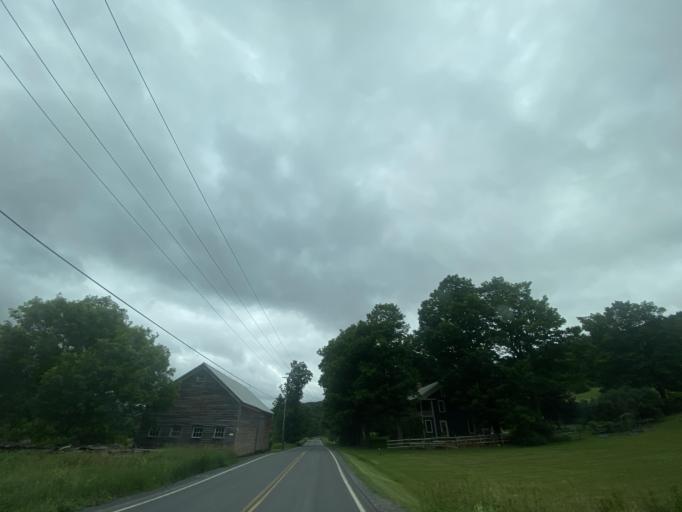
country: US
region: New York
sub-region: Schoharie County
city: Middleburgh
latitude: 42.3894
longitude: -74.3323
